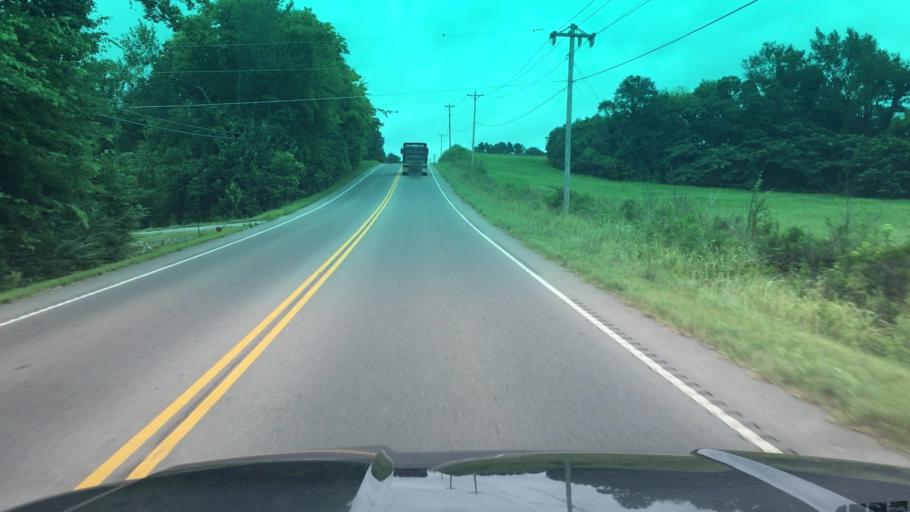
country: US
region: Tennessee
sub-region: Williamson County
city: Thompson's Station
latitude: 35.8127
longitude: -86.8520
